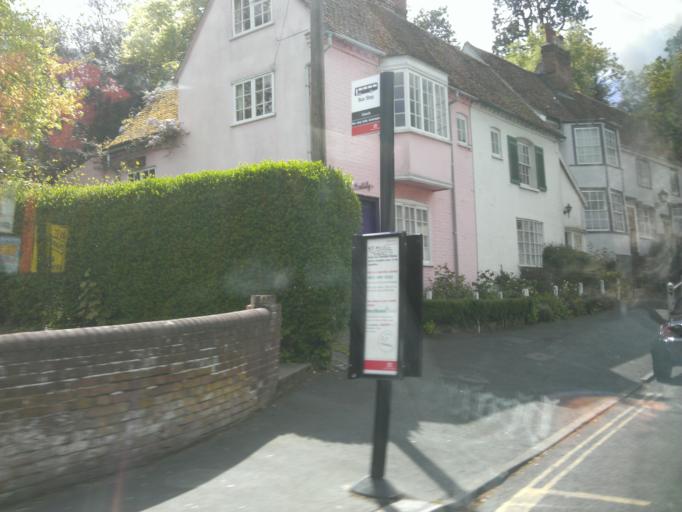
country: GB
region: England
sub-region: Essex
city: West Bergholt
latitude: 51.8901
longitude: 0.8633
